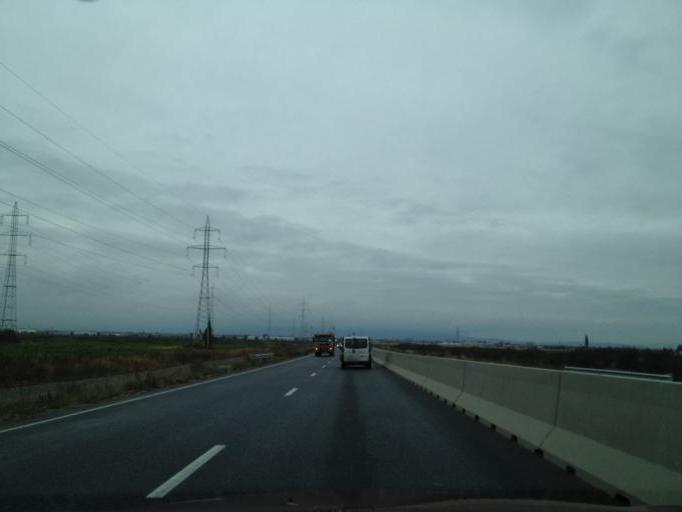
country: RO
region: Brasov
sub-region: Comuna Sanpetru
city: Sanpetru
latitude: 45.6916
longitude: 25.6086
